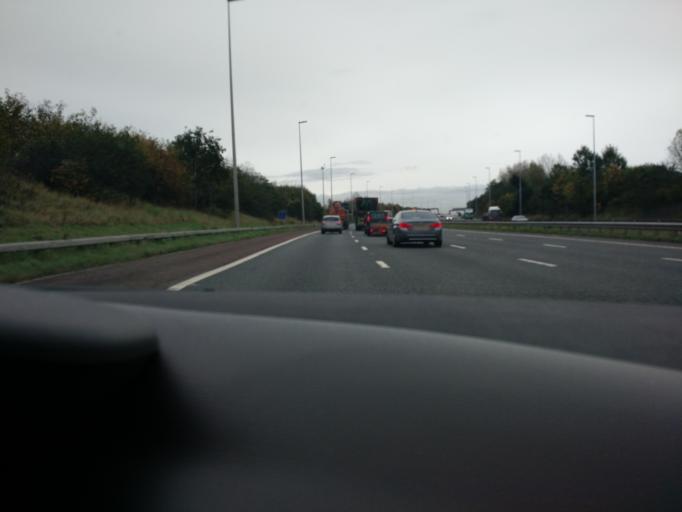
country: GB
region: England
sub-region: Lancashire
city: Goosnargh
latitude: 53.7926
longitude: -2.6676
